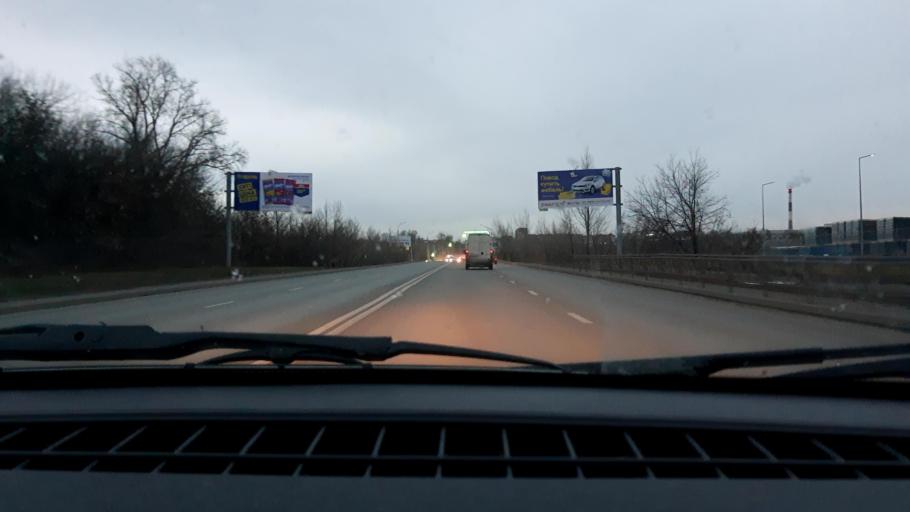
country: RU
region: Bashkortostan
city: Ufa
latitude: 54.7947
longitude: 56.0770
